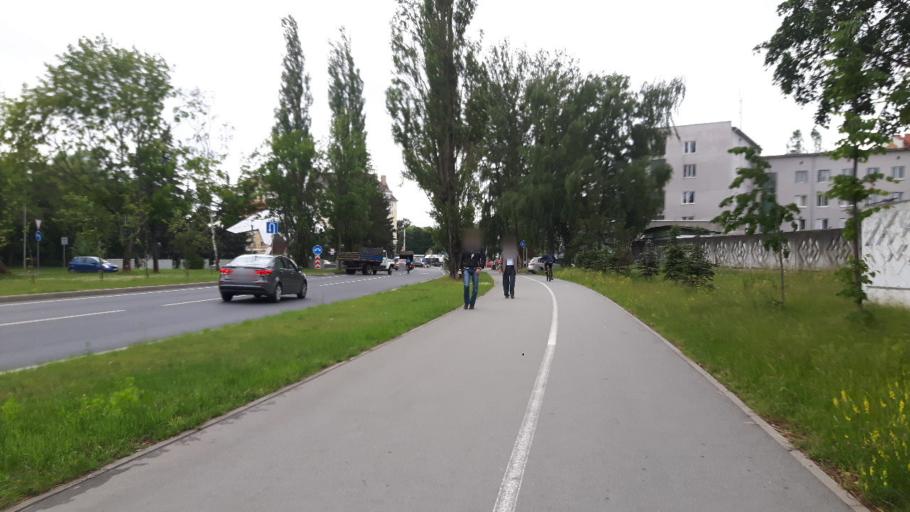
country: RU
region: Kaliningrad
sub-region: Gorod Kaliningrad
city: Kaliningrad
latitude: 54.7321
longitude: 20.4905
